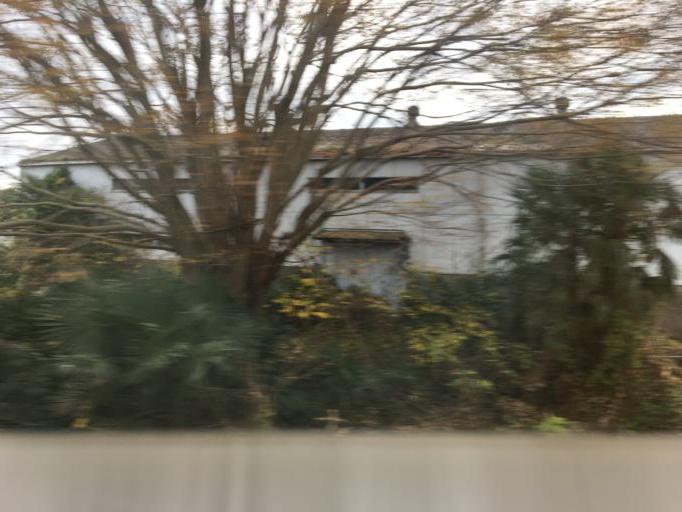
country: JP
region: Tochigi
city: Tochigi
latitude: 36.3641
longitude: 139.7564
